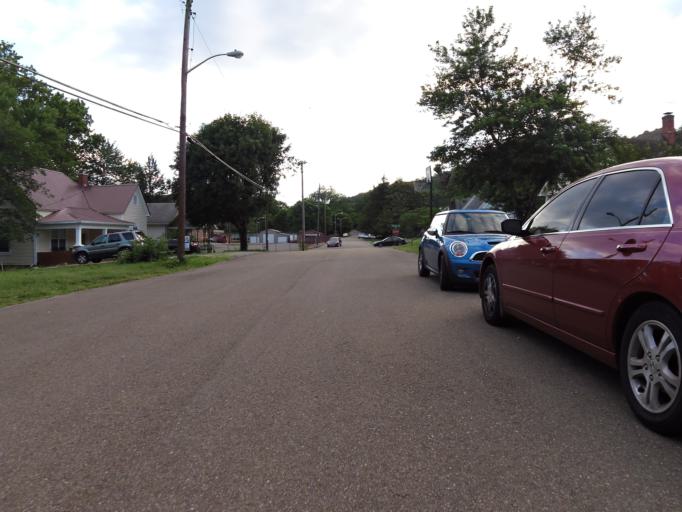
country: US
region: Tennessee
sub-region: Knox County
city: Knoxville
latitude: 36.0011
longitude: -83.9363
